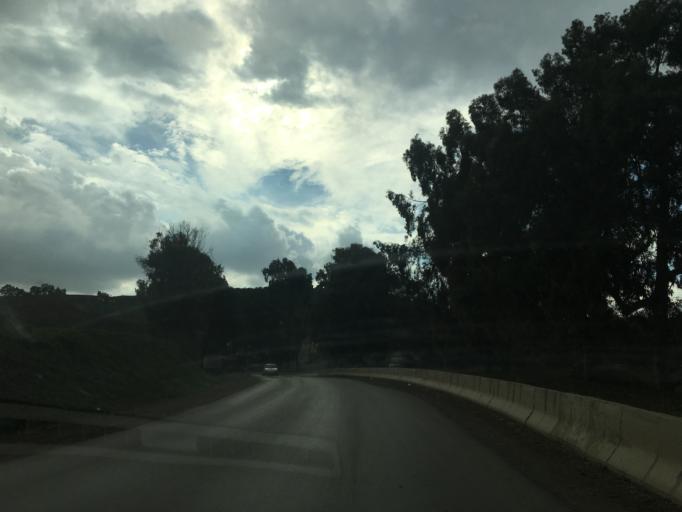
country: DZ
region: Bouira
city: Bouira
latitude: 36.3465
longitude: 3.8849
